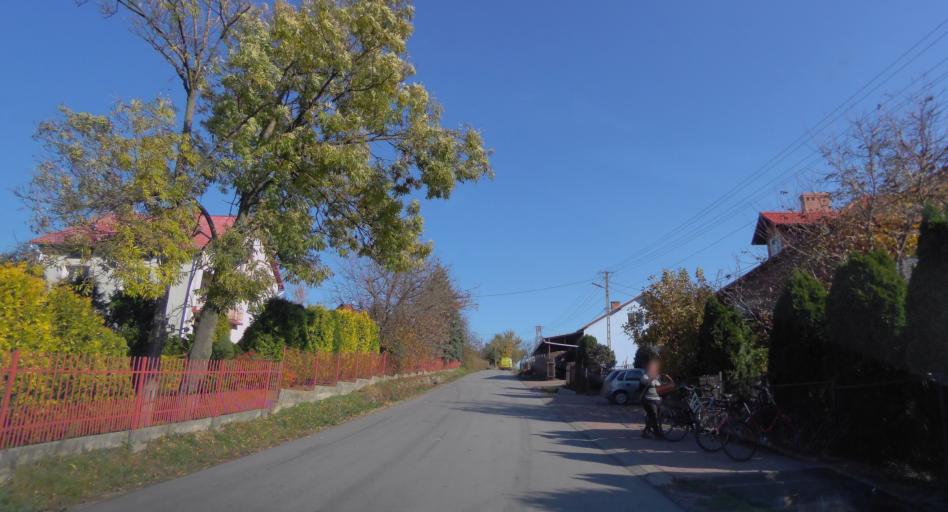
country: PL
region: Subcarpathian Voivodeship
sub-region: Powiat lezajski
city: Wola Zarczycka
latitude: 50.2790
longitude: 22.2676
